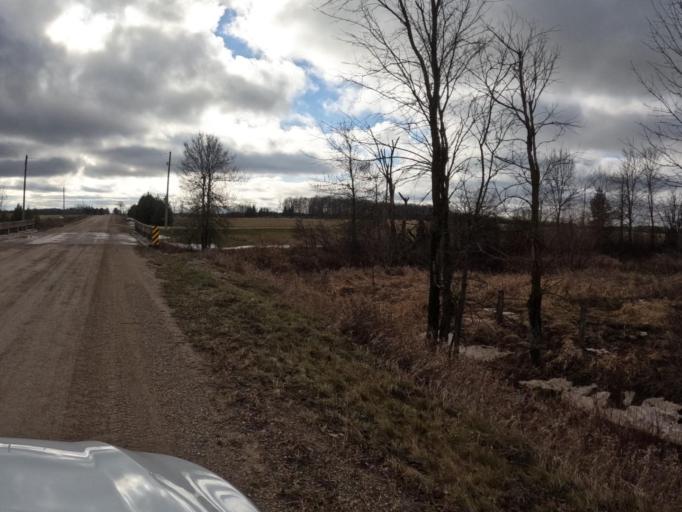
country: CA
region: Ontario
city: Shelburne
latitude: 43.9837
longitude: -80.3830
